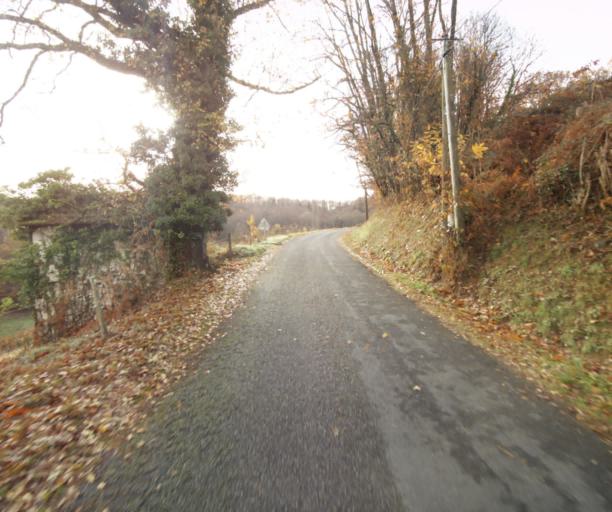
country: FR
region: Limousin
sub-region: Departement de la Correze
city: Cornil
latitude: 45.2173
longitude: 1.7157
